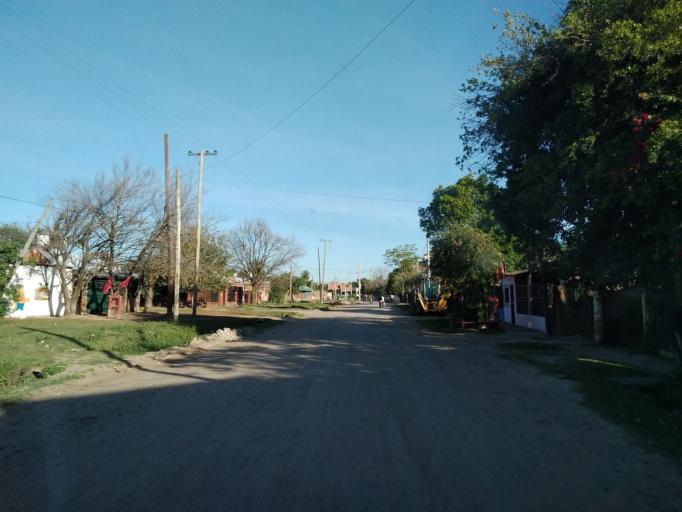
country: AR
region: Corrientes
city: Corrientes
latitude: -27.4994
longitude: -58.8366
